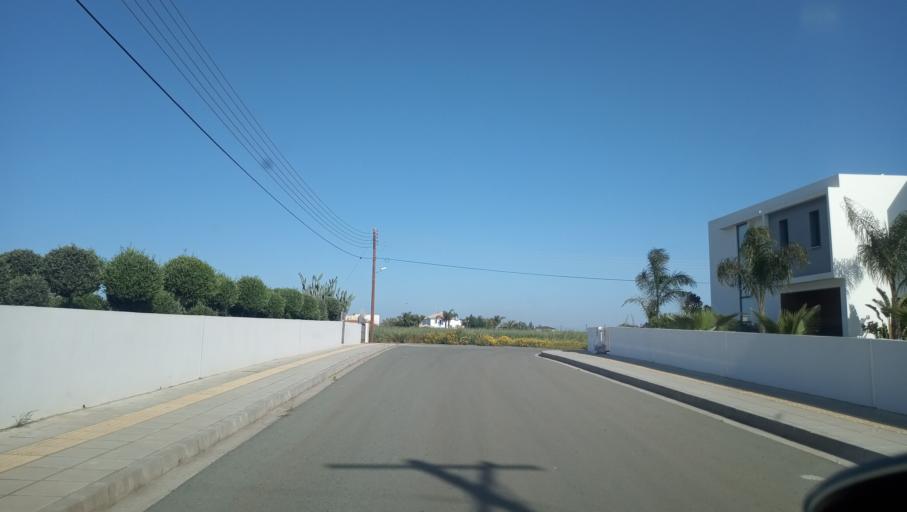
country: CY
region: Lefkosia
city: Tseri
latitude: 35.0782
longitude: 33.3181
